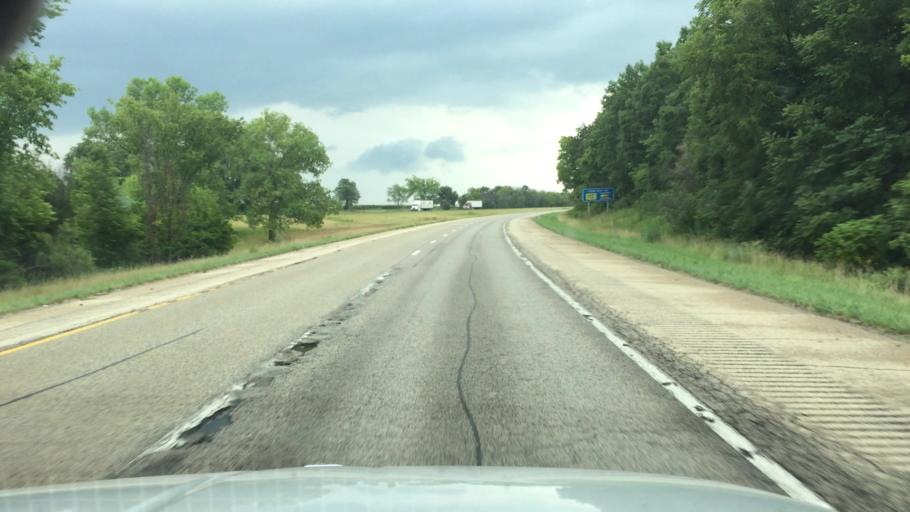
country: US
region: Illinois
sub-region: Peoria County
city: Hanna City
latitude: 40.7879
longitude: -89.7817
